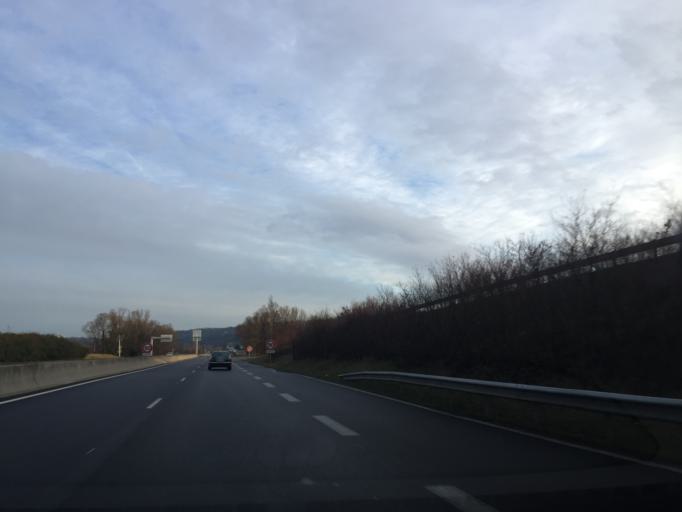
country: FR
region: Rhone-Alpes
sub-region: Departement de l'Isere
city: L'Isle-d'Abeau
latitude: 45.6072
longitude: 5.2287
